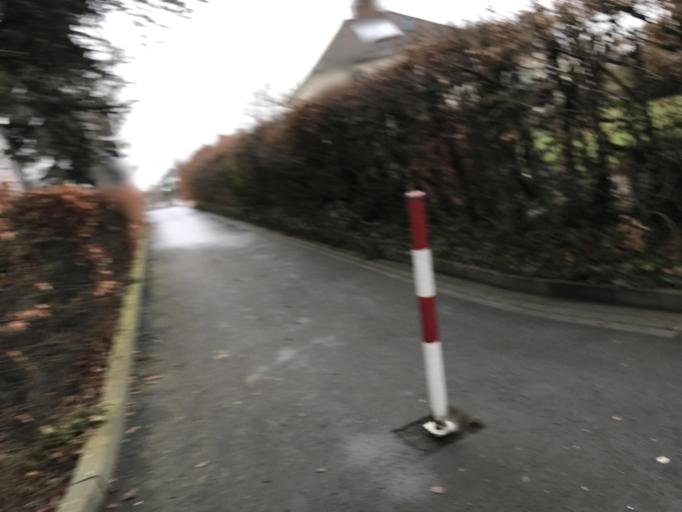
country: DE
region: Hesse
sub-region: Regierungsbezirk Kassel
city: Bad Wildungen
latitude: 51.1129
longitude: 9.1175
